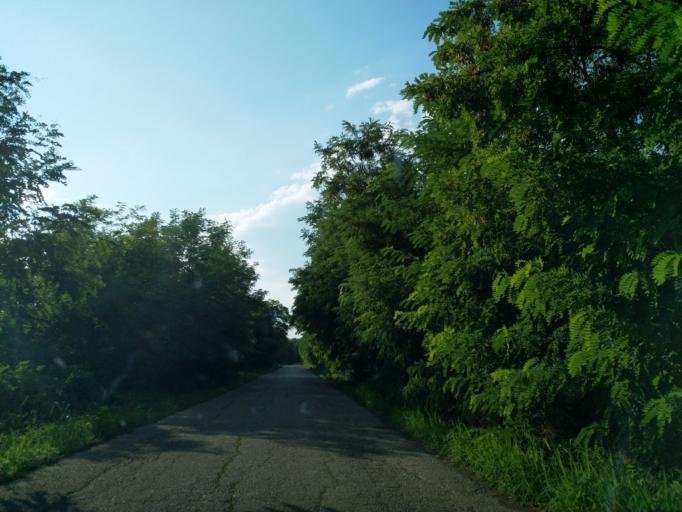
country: RS
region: Central Serbia
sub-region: Pomoravski Okrug
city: Jagodina
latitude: 43.9980
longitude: 21.1912
